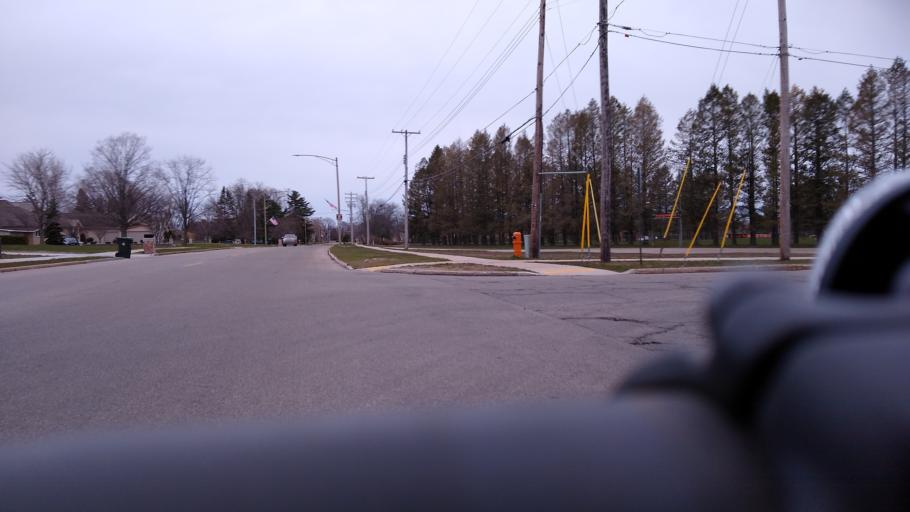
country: US
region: Michigan
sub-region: Delta County
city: Escanaba
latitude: 45.7246
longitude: -87.0679
